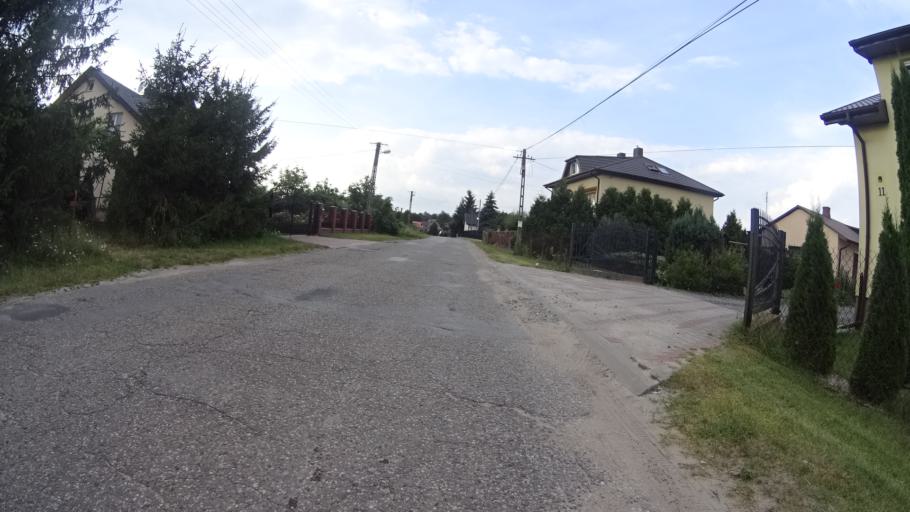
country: PL
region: Masovian Voivodeship
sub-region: Powiat grojecki
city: Mogielnica
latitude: 51.6709
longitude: 20.7406
